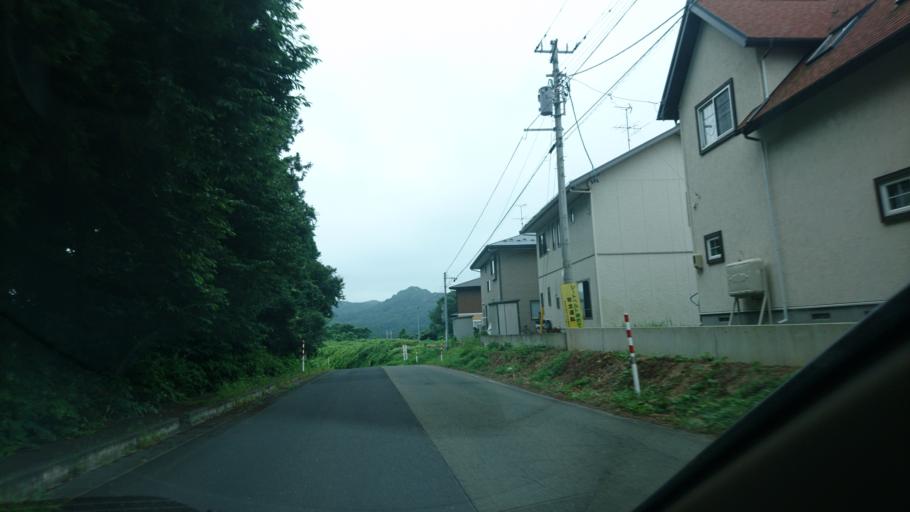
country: JP
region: Iwate
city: Kitakami
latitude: 39.2652
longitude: 141.1107
